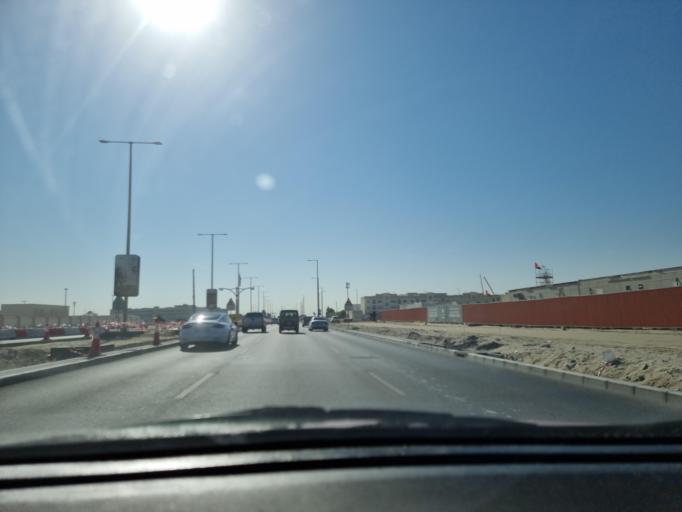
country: AE
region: Abu Dhabi
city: Abu Dhabi
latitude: 24.4178
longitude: 54.5673
